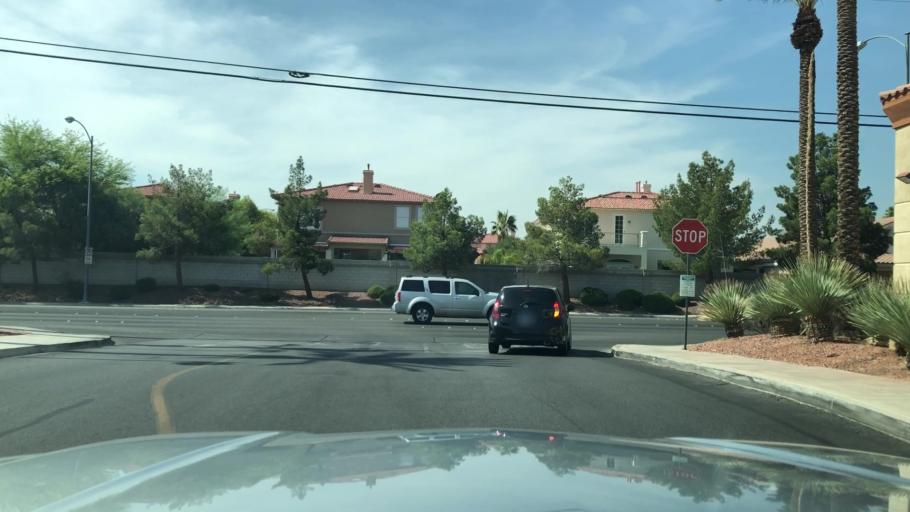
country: US
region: Nevada
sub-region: Clark County
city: Whitney
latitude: 36.0209
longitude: -115.1251
